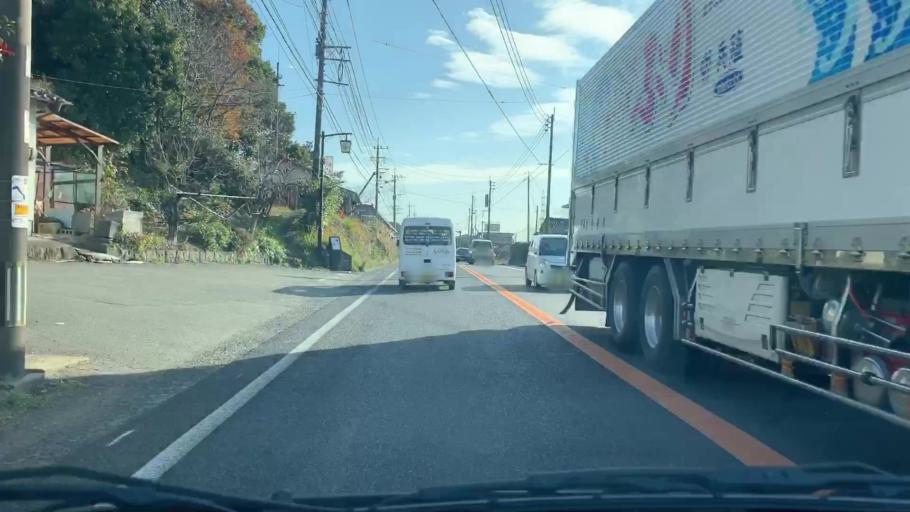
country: JP
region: Saga Prefecture
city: Takeocho-takeo
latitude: 33.2155
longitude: 130.0906
